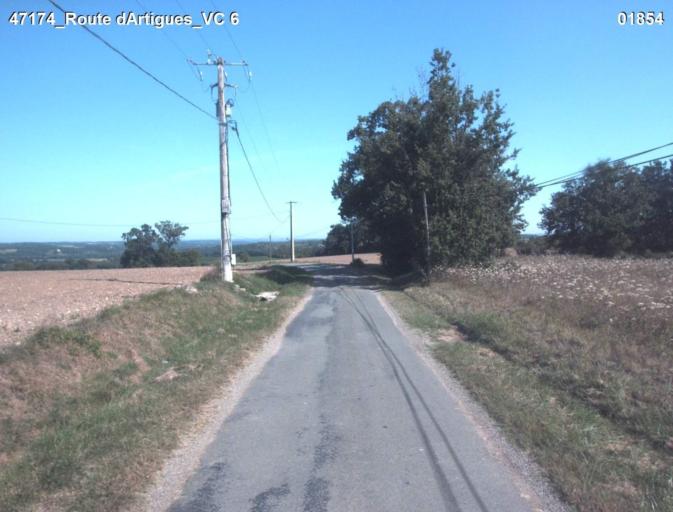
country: FR
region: Midi-Pyrenees
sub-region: Departement du Gers
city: Condom
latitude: 44.0235
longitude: 0.3339
